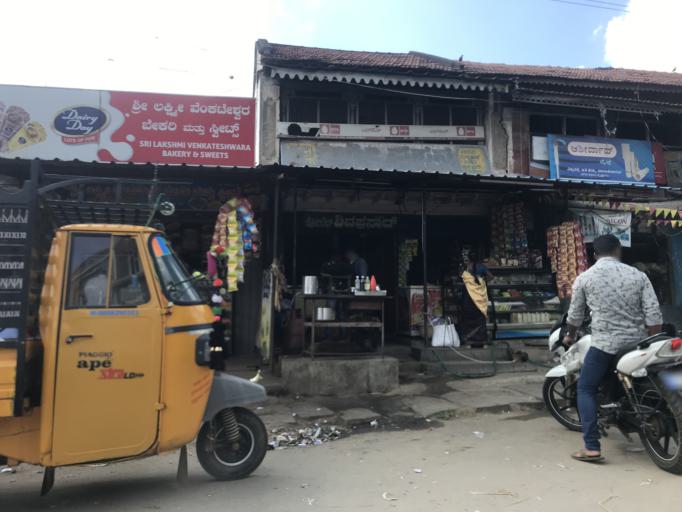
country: IN
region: Karnataka
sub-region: Mandya
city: Krishnarajpet
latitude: 12.7617
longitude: 76.4258
